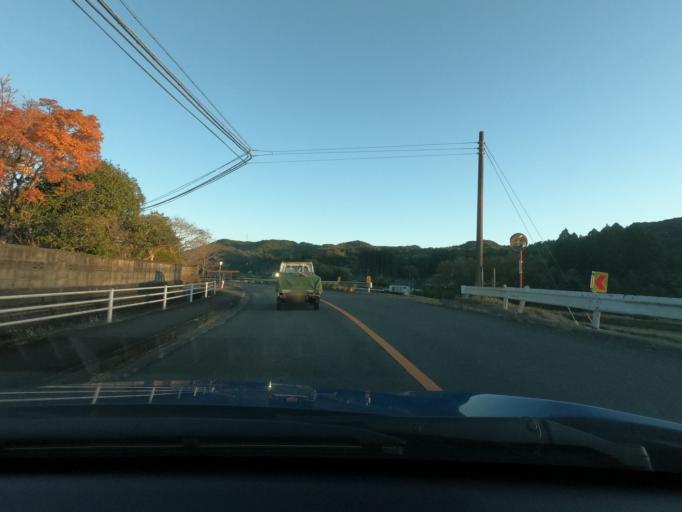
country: JP
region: Kagoshima
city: Satsumasendai
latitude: 31.7923
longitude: 130.4513
